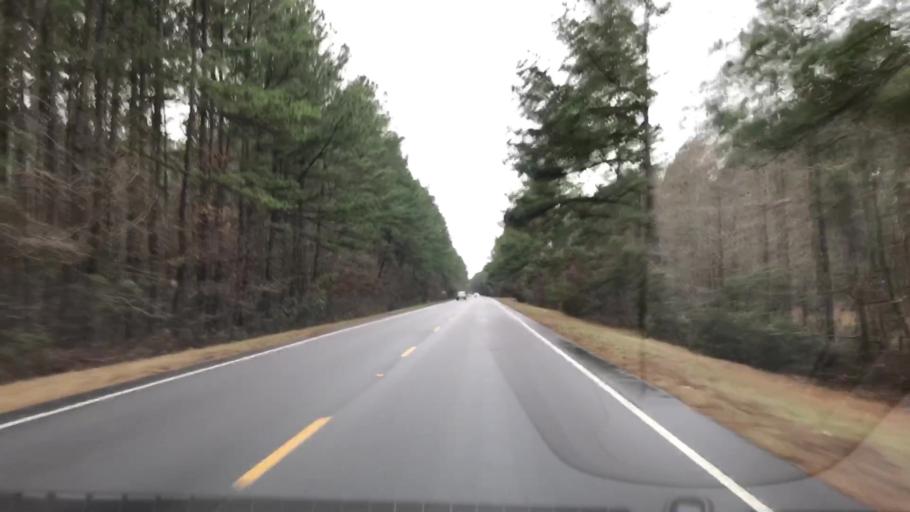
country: US
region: South Carolina
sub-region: Berkeley County
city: Saint Stephen
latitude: 33.2902
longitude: -79.7909
